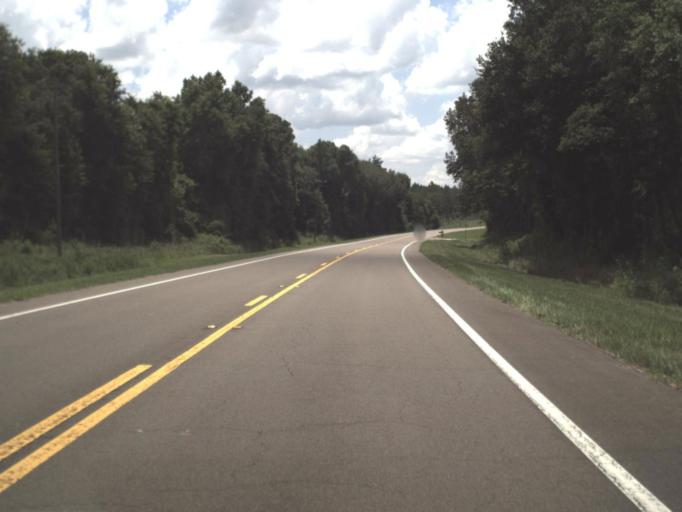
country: US
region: Florida
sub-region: Alachua County
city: Alachua
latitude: 29.8231
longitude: -82.3891
